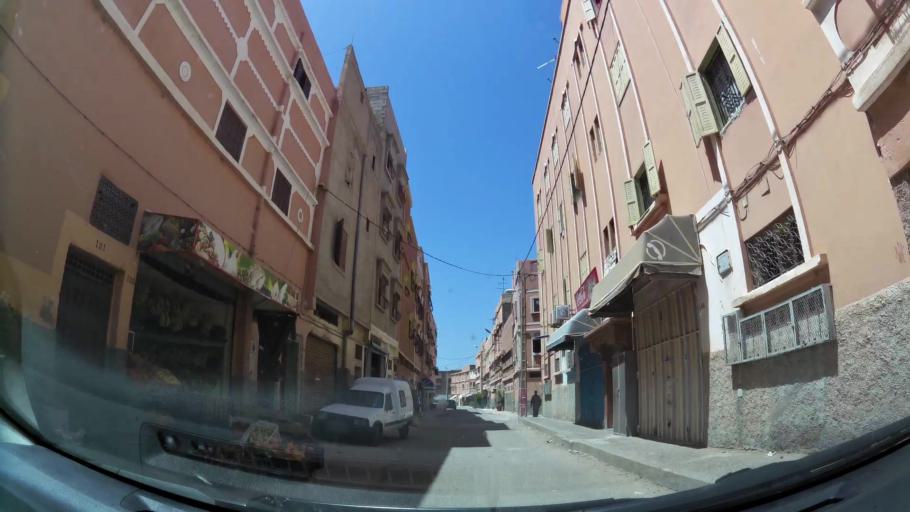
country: MA
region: Souss-Massa-Draa
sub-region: Inezgane-Ait Mellou
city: Inezgane
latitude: 30.3442
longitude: -9.4963
